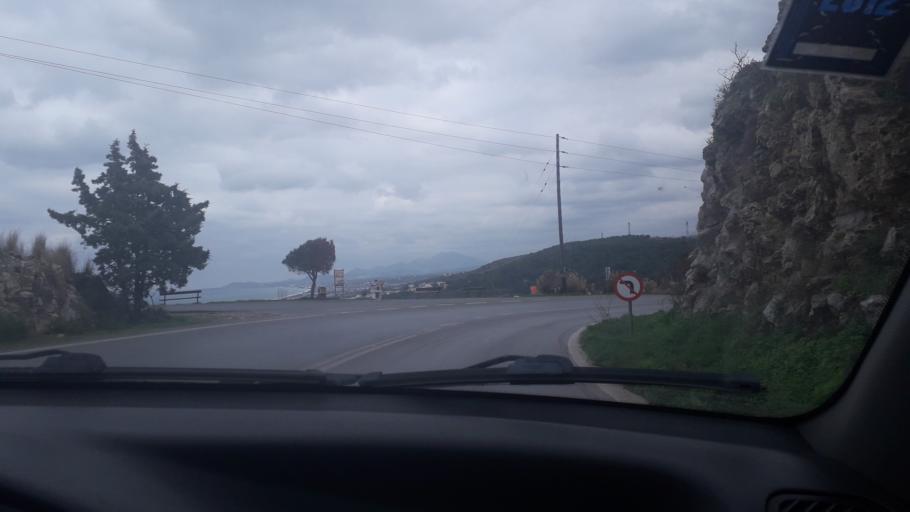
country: GR
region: Crete
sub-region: Nomos Rethymnis
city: Rethymno
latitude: 35.3590
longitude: 24.4687
